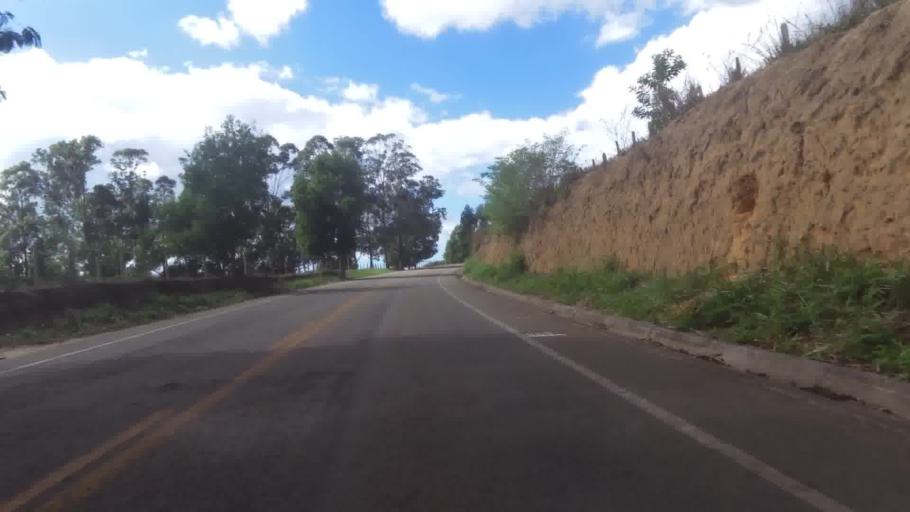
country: BR
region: Espirito Santo
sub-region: Marataizes
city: Marataizes
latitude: -21.1140
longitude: -41.0277
